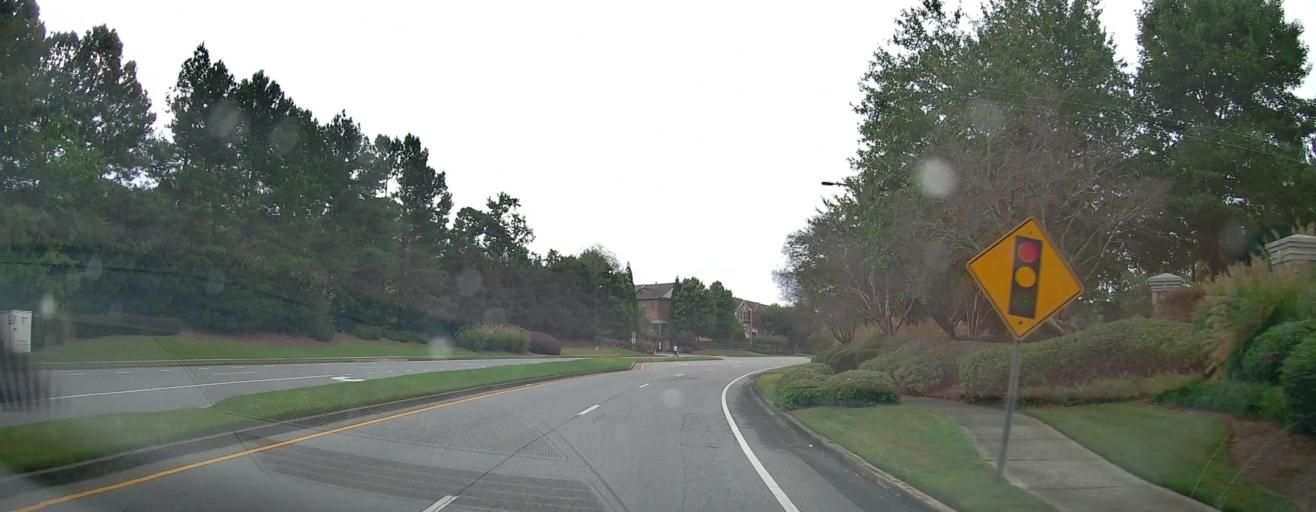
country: US
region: Georgia
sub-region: Fulton County
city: Alpharetta
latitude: 34.0998
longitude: -84.2645
